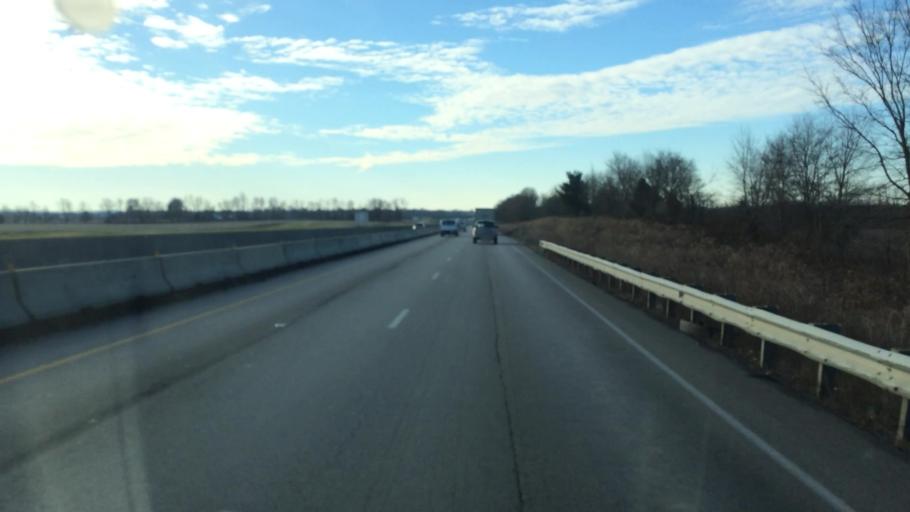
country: US
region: Kentucky
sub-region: Hardin County
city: Elizabethtown
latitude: 37.5822
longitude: -85.8720
